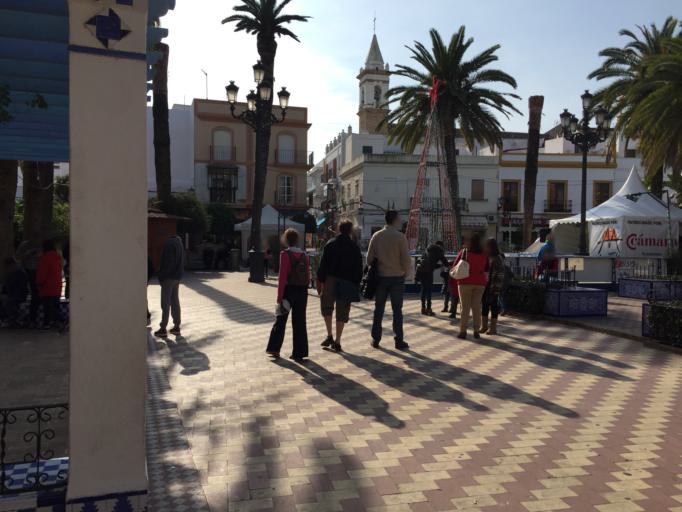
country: ES
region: Andalusia
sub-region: Provincia de Huelva
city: Ayamonte
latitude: 37.2142
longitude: -7.4086
